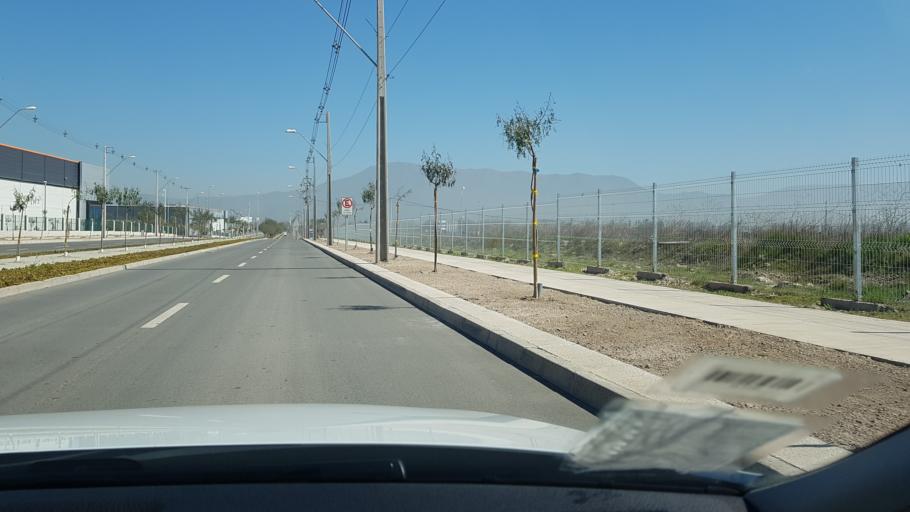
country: CL
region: Santiago Metropolitan
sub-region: Provincia de Santiago
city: Lo Prado
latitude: -33.4259
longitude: -70.7913
